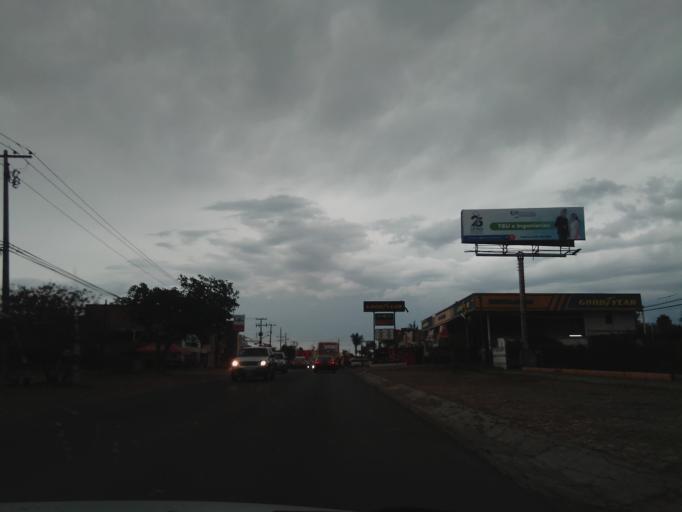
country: MX
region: Guanajuato
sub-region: Dolores Hidalgo Cuna de la Independencia Nacional
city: Dolores Hidalgo Cuna de la Independencia Nacional
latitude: 21.1573
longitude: -100.9236
